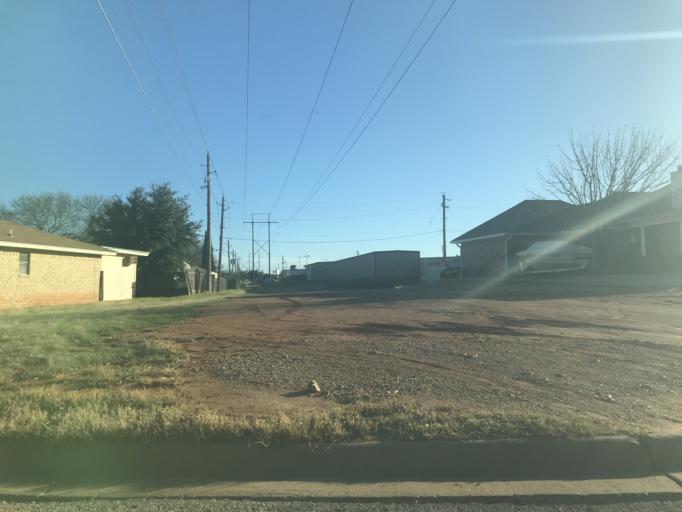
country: US
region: Texas
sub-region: Tom Green County
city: San Angelo
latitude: 31.4307
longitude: -100.4952
